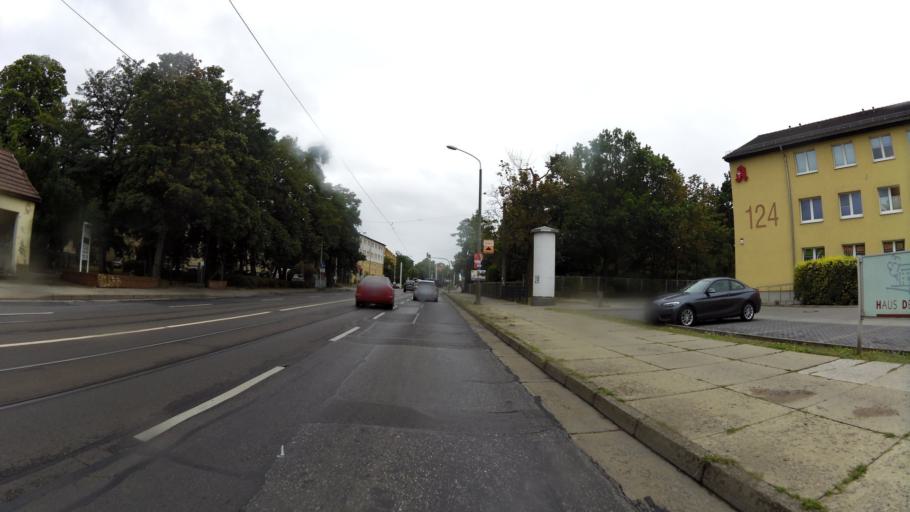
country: DE
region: Brandenburg
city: Cottbus
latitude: 51.7453
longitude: 14.3275
